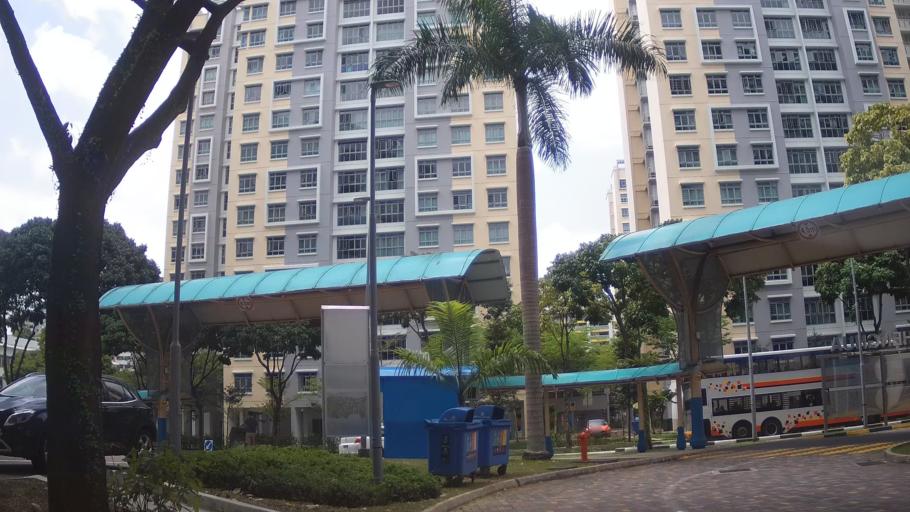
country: MY
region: Johor
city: Johor Bahru
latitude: 1.3881
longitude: 103.7723
